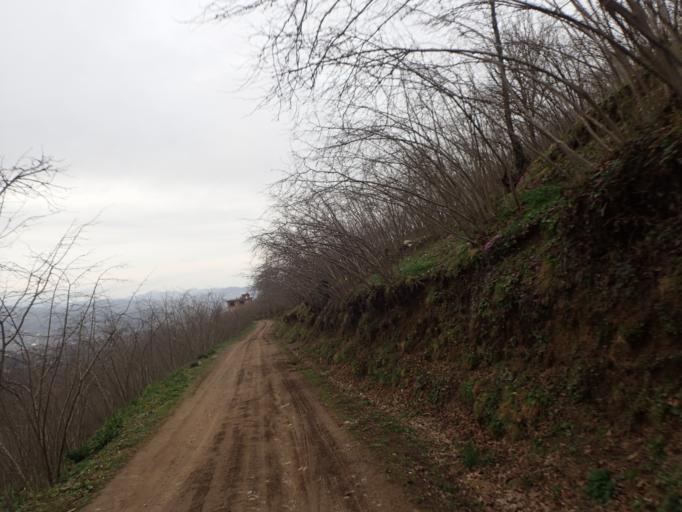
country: TR
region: Ordu
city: Camas
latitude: 40.9131
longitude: 37.5186
